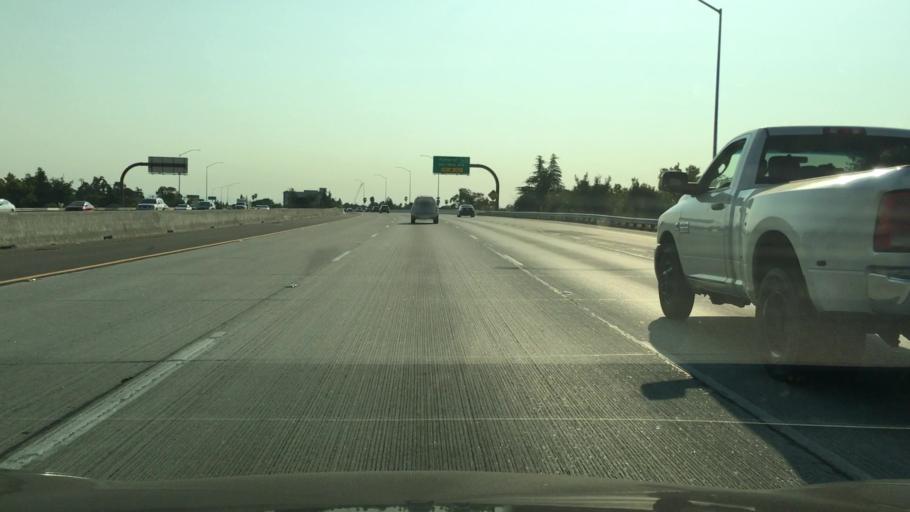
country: US
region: California
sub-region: Fresno County
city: Fresno
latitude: 36.7515
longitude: -119.7933
